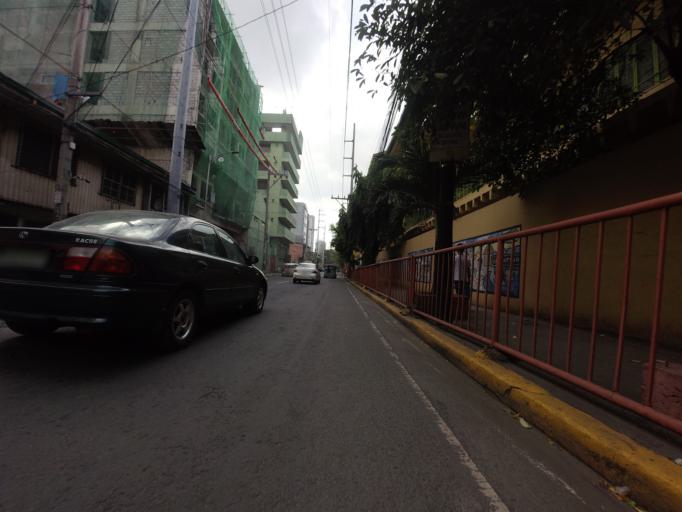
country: PH
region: Metro Manila
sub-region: City of Manila
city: Quiapo
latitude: 14.5811
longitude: 120.9935
